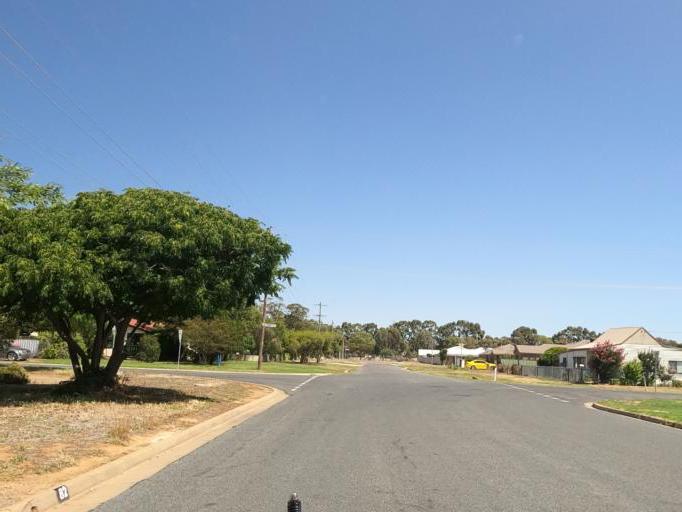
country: AU
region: New South Wales
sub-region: Corowa Shire
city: Mulwala
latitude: -35.9855
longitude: 145.9991
